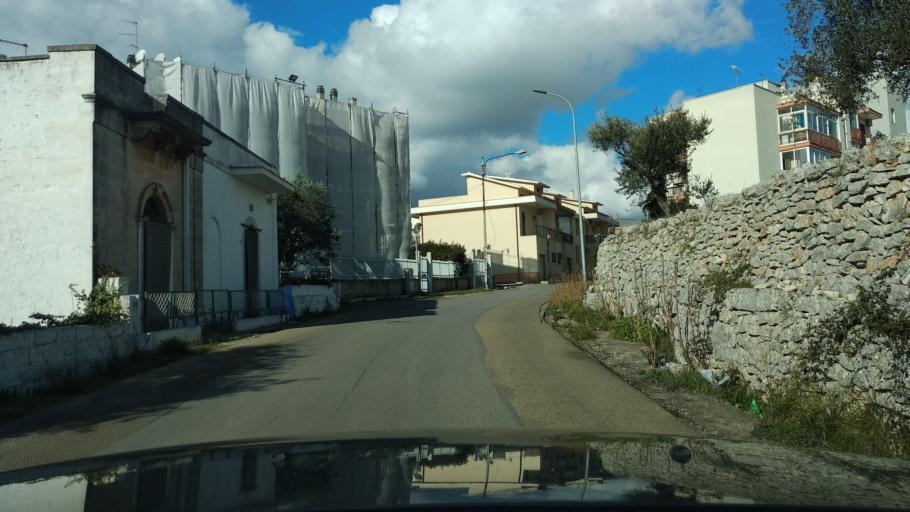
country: IT
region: Apulia
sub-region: Provincia di Brindisi
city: Cisternino
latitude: 40.7387
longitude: 17.4312
